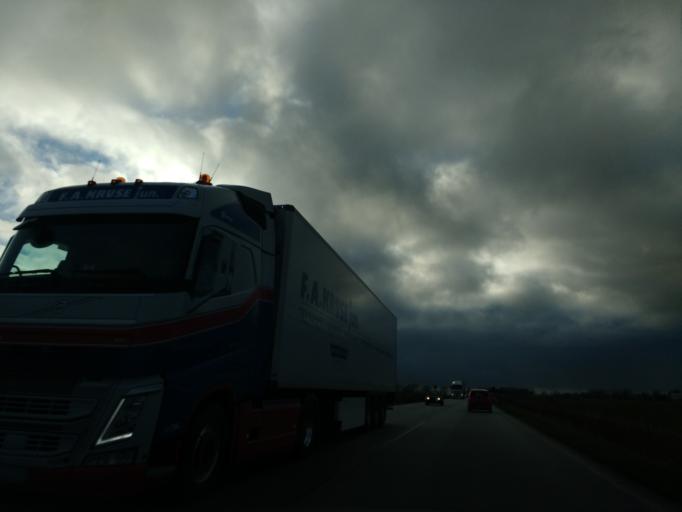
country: DE
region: Schleswig-Holstein
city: Stordorf
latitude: 53.9216
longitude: 9.4010
